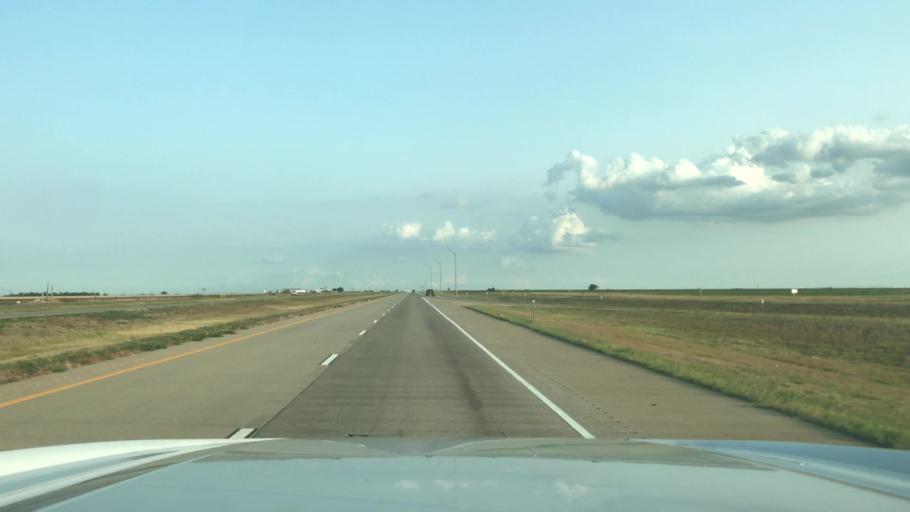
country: US
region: Texas
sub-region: Hale County
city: Seth Ward
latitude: 34.3394
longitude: -101.7436
